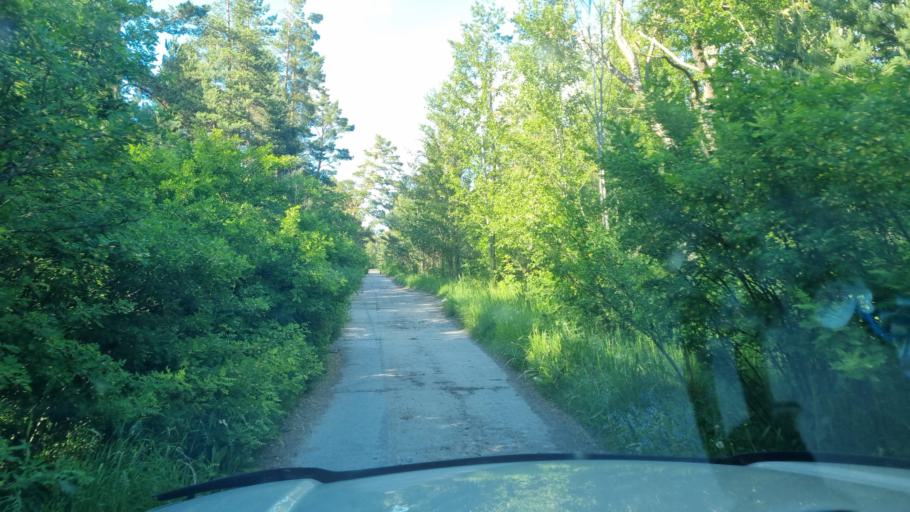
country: LV
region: Ventspils
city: Ventspils
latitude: 57.3644
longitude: 21.5131
